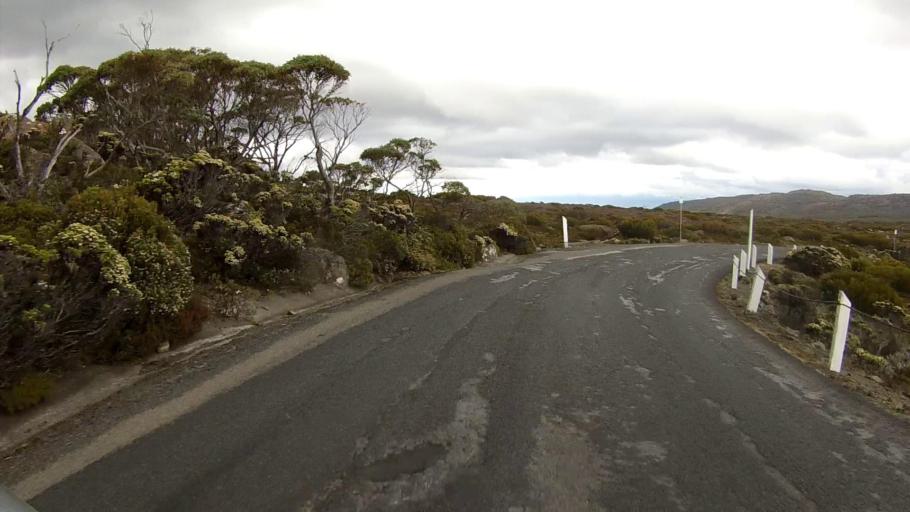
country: AU
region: Tasmania
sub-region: Glenorchy
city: West Moonah
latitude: -42.8923
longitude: 147.2260
